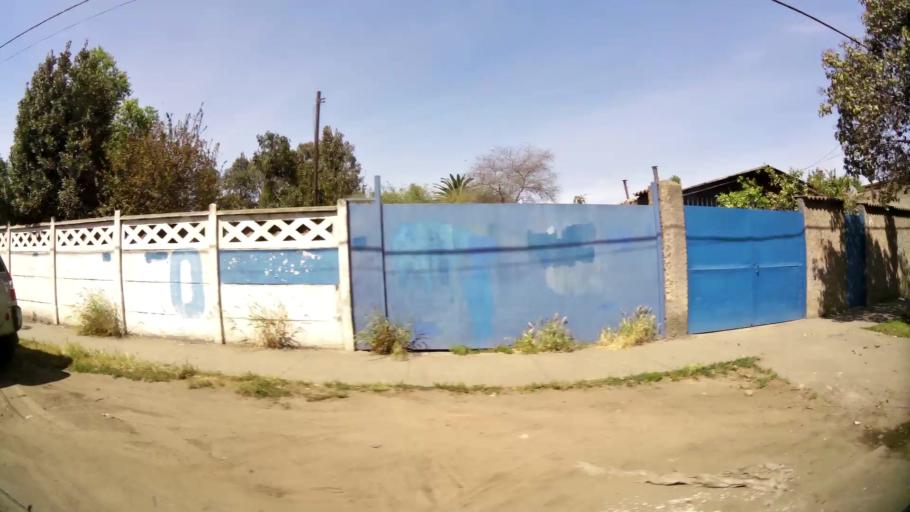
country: CL
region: Santiago Metropolitan
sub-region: Provincia de Maipo
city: San Bernardo
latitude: -33.5349
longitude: -70.6949
